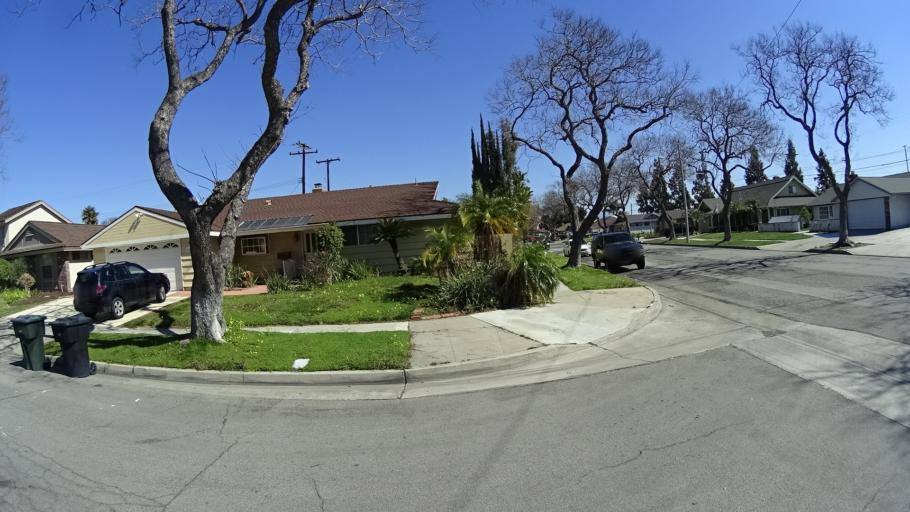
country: US
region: California
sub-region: Orange County
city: Placentia
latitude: 33.8333
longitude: -117.8736
